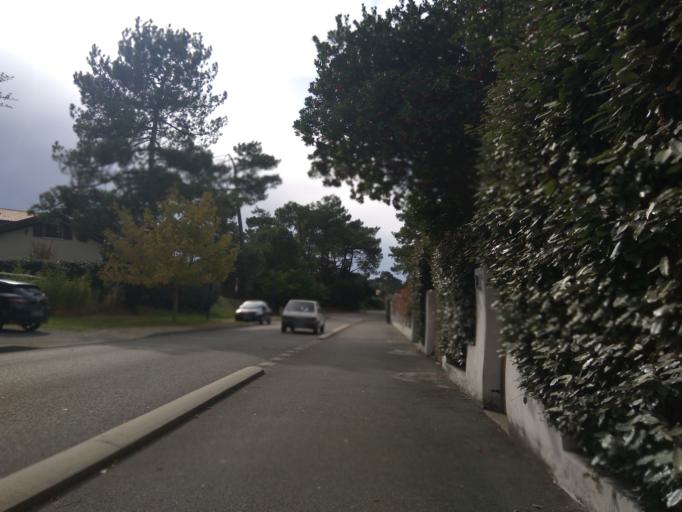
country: FR
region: Aquitaine
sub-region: Departement des Landes
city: Capbreton
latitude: 43.6370
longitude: -1.4391
